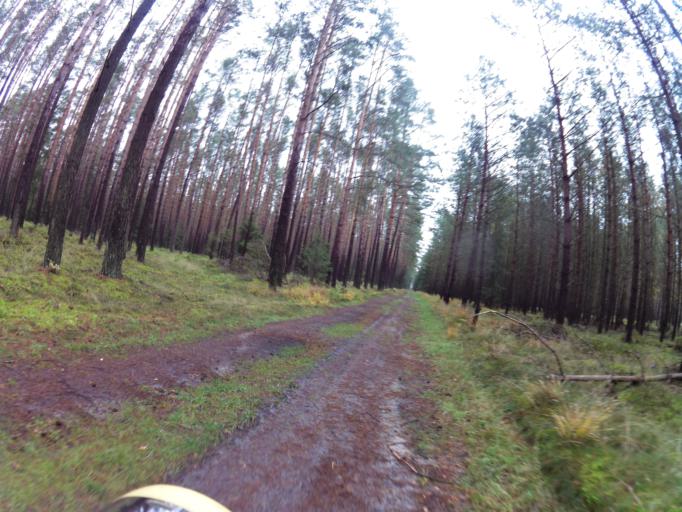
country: PL
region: West Pomeranian Voivodeship
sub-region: Powiat policki
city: Dobra
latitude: 53.6059
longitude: 14.3438
